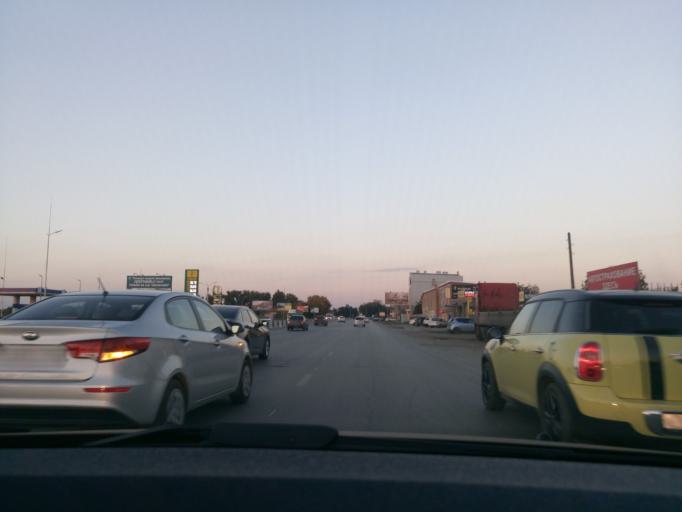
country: RU
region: Rostov
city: Severnyy
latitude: 47.2570
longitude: 39.6176
